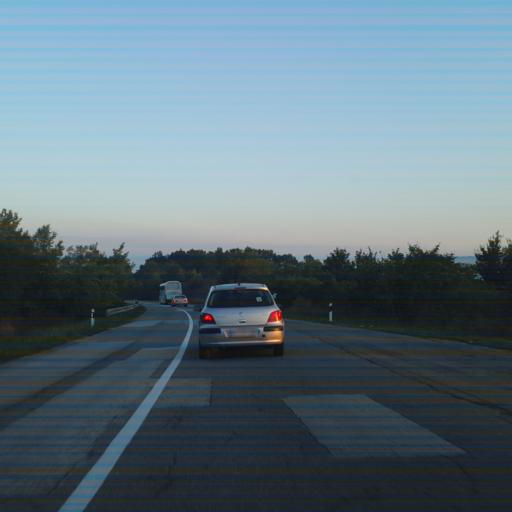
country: RS
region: Central Serbia
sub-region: Zajecarski Okrug
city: Zajecar
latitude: 43.9613
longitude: 22.2993
